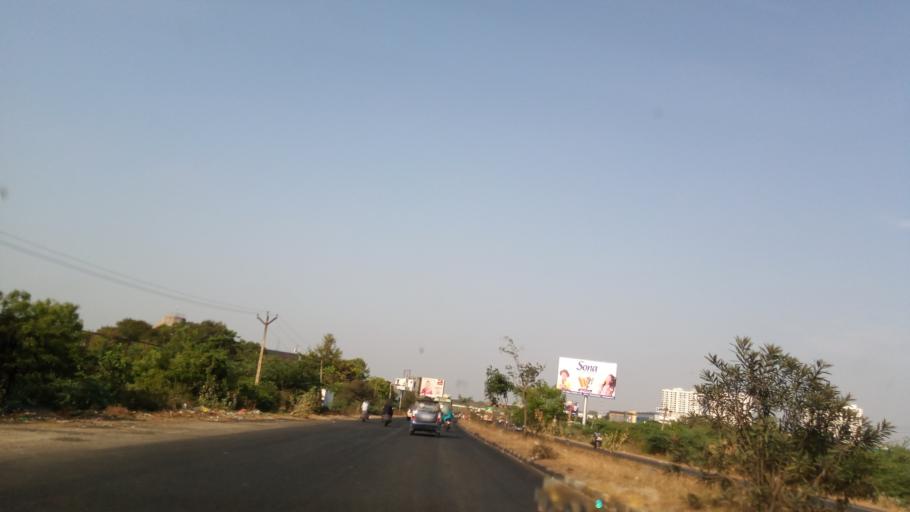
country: IN
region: Tamil Nadu
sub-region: Kancheepuram
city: Nandambakkam
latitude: 13.0346
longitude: 80.0405
